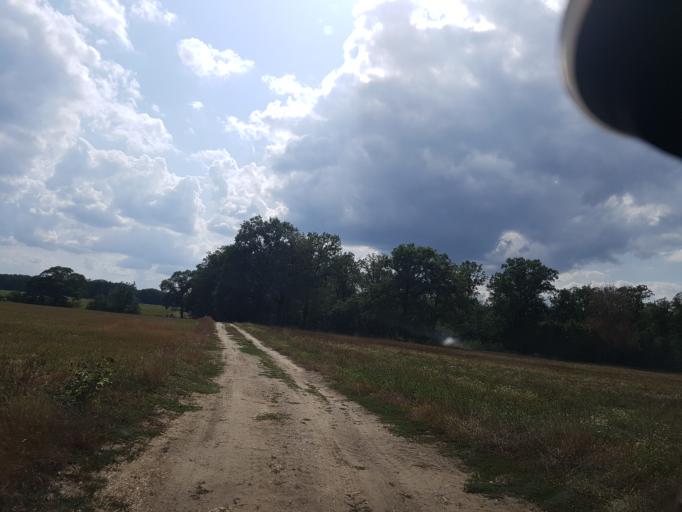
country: DE
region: Brandenburg
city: Calau
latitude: 51.7703
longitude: 13.9688
